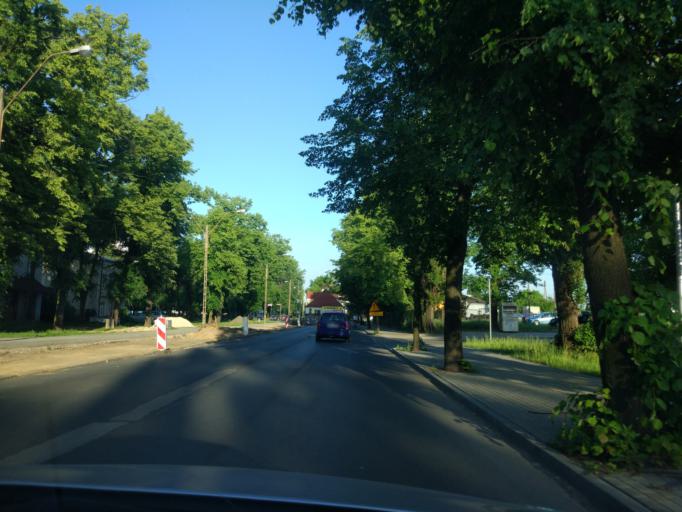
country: PL
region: Lodz Voivodeship
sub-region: Powiat kutnowski
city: Kutno
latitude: 52.2272
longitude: 19.3504
